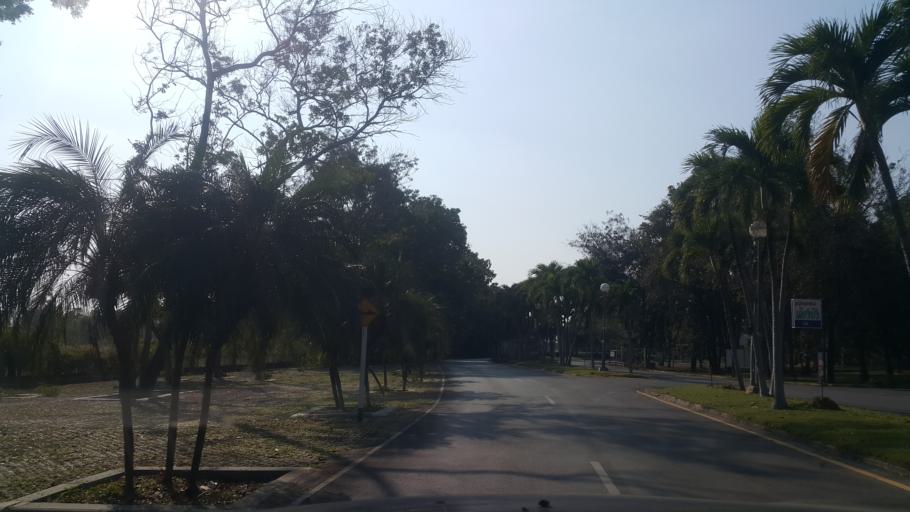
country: TH
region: Nakhon Ratchasima
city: Nakhon Ratchasima
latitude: 14.8501
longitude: 102.0768
